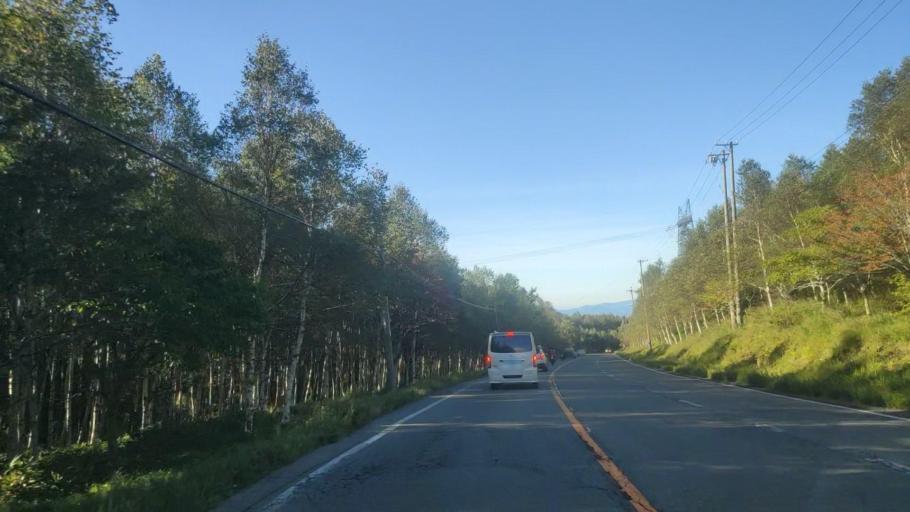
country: JP
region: Nagano
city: Kamimaruko
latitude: 36.1567
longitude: 138.2792
